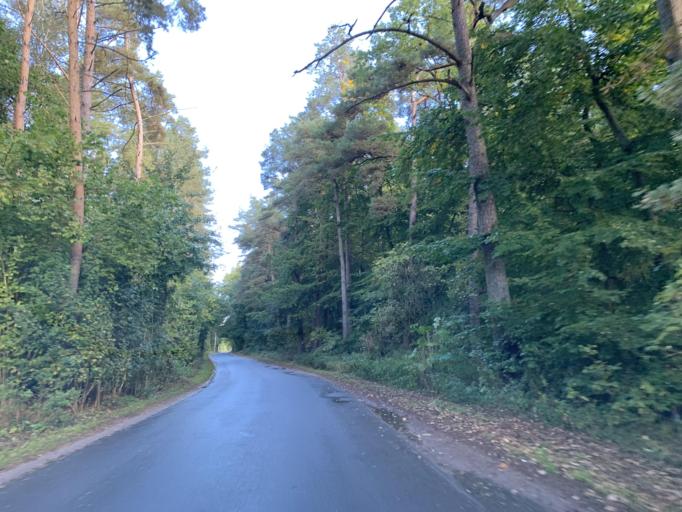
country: DE
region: Mecklenburg-Vorpommern
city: Blankensee
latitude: 53.4310
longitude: 13.2636
